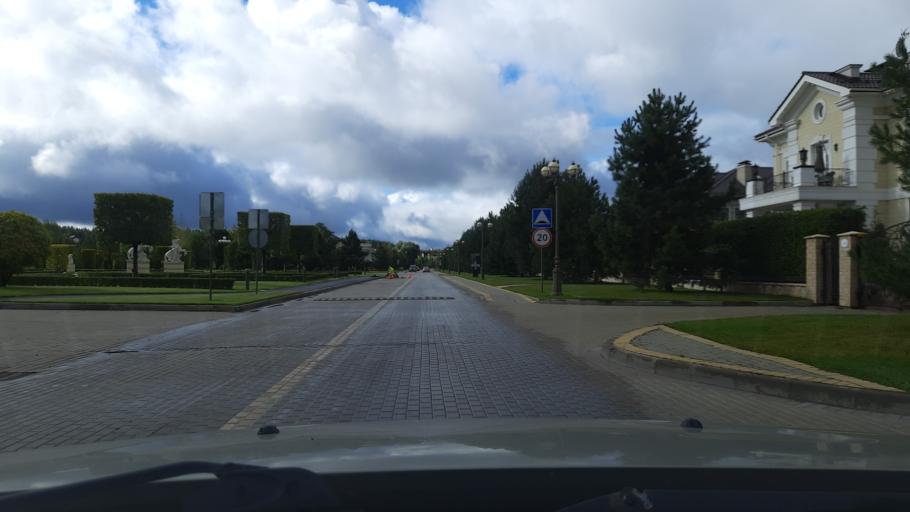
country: RU
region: Moskovskaya
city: Nikolina Gora
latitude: 55.7777
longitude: 37.0540
